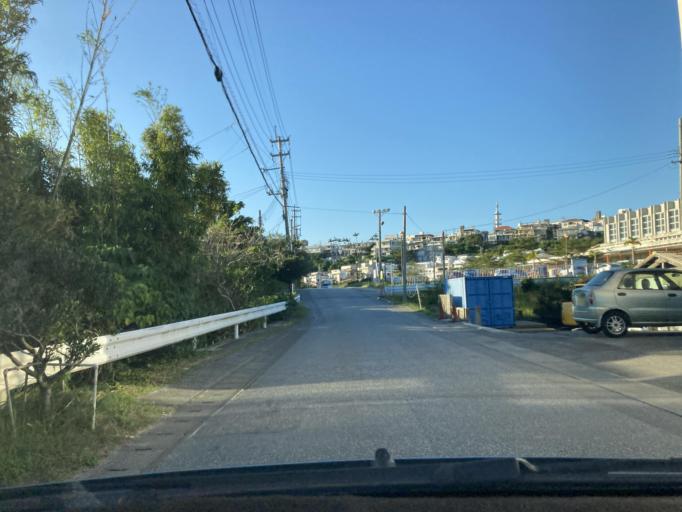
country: JP
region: Okinawa
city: Naha-shi
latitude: 26.2130
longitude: 127.7288
